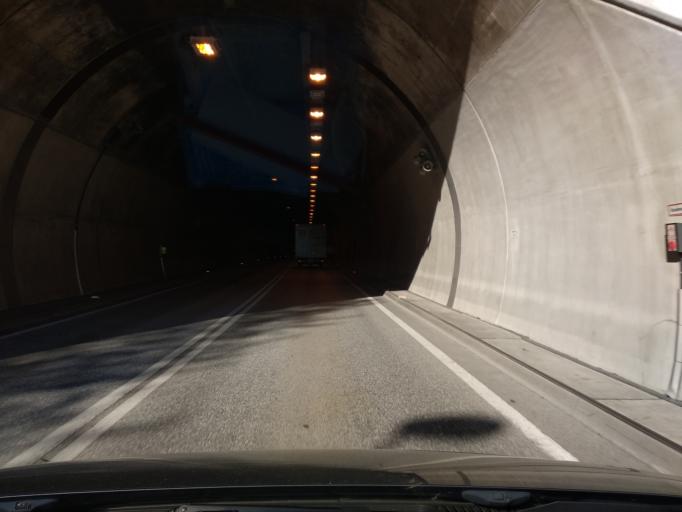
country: AT
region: Tyrol
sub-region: Politischer Bezirk Schwaz
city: Strass im Zillertal
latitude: 47.3866
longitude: 11.8266
